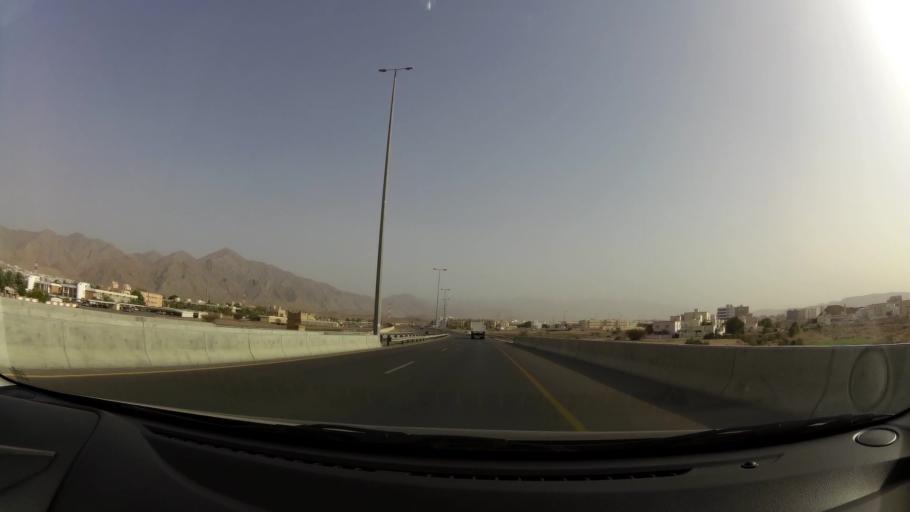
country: OM
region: Muhafazat Masqat
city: Bawshar
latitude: 23.5515
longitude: 58.3669
